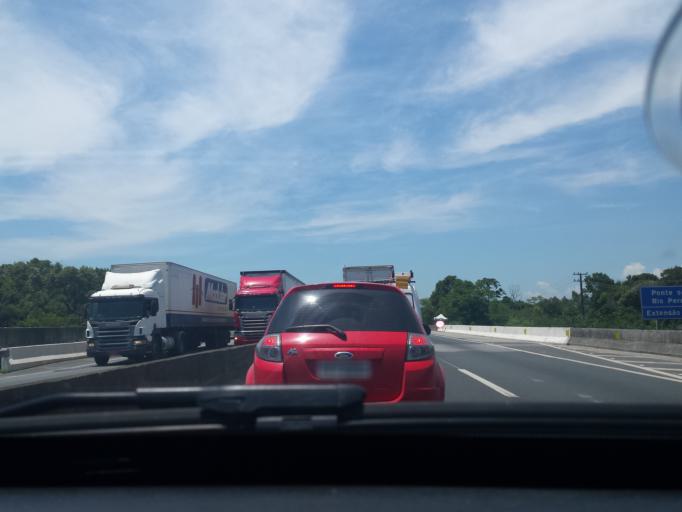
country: BR
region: Santa Catarina
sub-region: Itapema
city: Itapema
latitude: -27.1357
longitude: -48.6100
